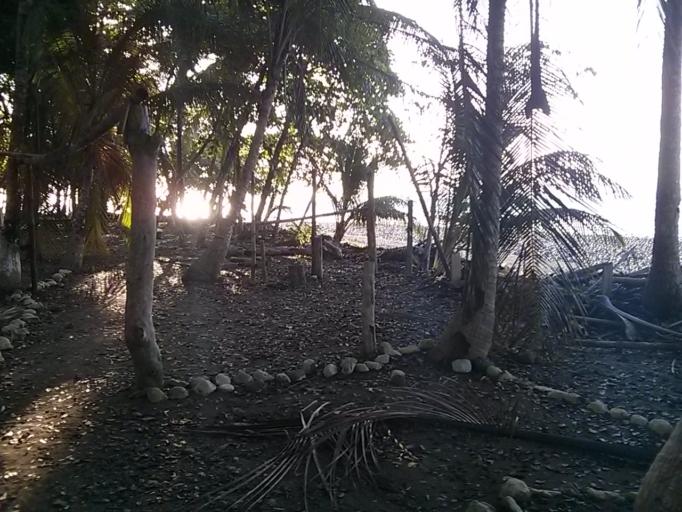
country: CR
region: Puntarenas
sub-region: Canton de Golfito
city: Golfito
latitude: 8.3956
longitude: -83.1366
